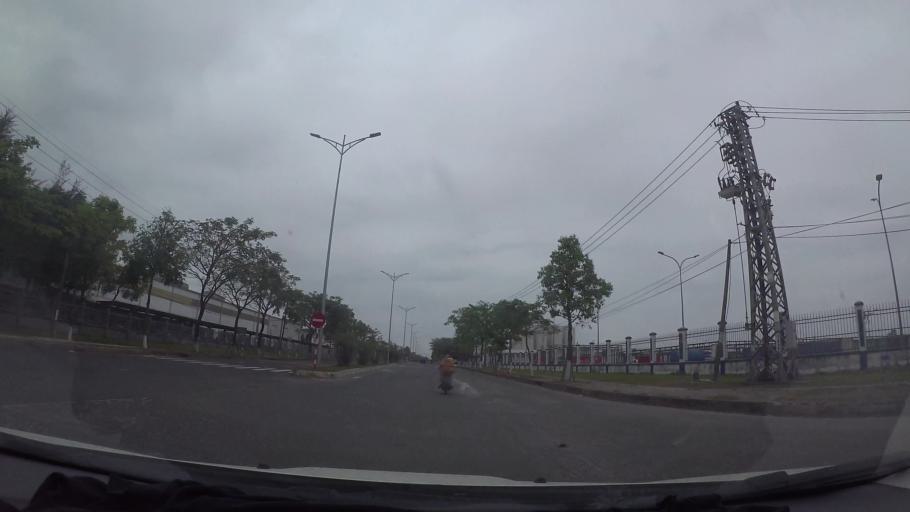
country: VN
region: Da Nang
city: Lien Chieu
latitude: 16.0773
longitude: 108.1400
